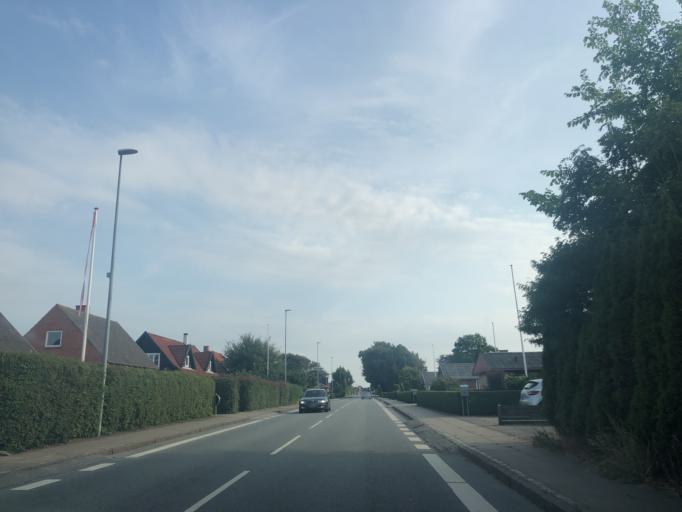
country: DK
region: Central Jutland
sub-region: Skive Kommune
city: Skive
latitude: 56.6197
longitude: 8.8801
